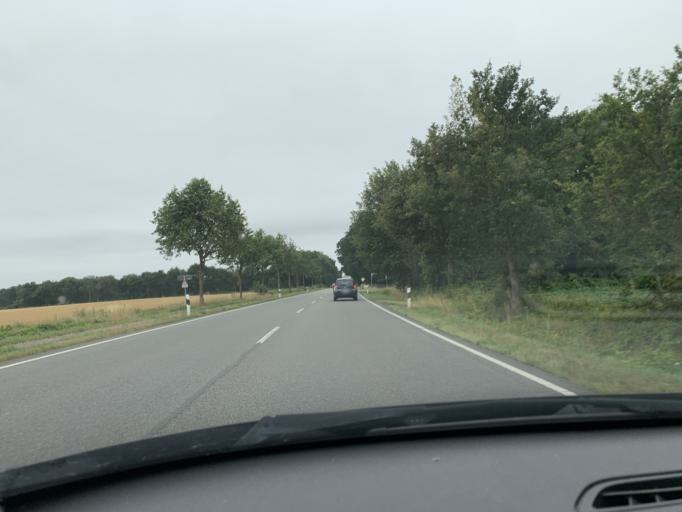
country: DE
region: Lower Saxony
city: Bawinkel
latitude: 52.5750
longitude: 7.3744
